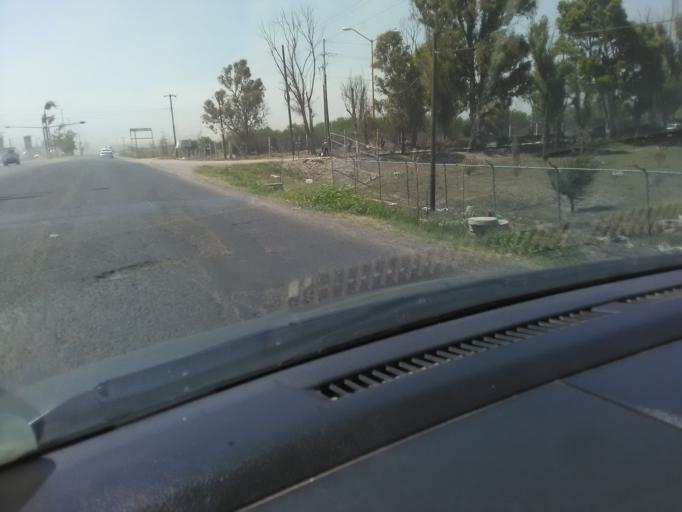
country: MX
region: Durango
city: Victoria de Durango
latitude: 24.0281
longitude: -104.5911
